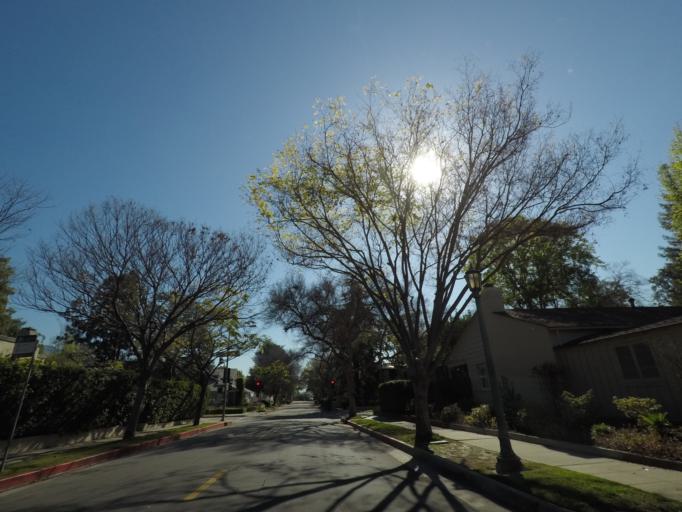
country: US
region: California
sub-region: Los Angeles County
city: La Canada Flintridge
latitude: 34.1714
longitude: -118.1774
